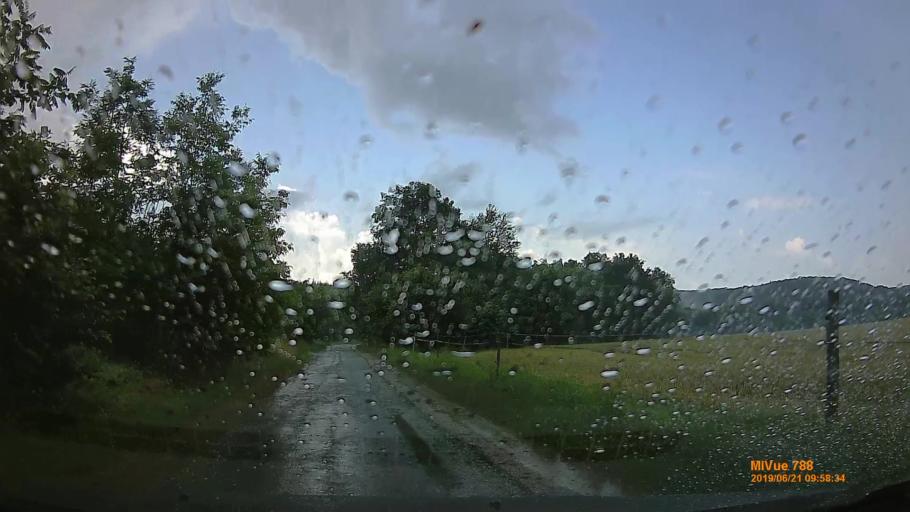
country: HU
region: Baranya
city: Buekkoesd
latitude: 46.2157
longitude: 17.9725
